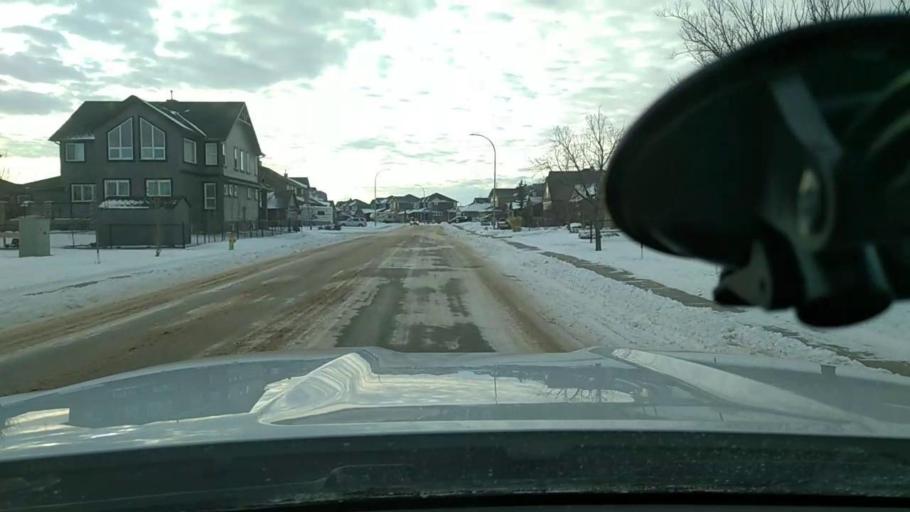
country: CA
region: Alberta
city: Chestermere
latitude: 50.9643
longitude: -113.6628
